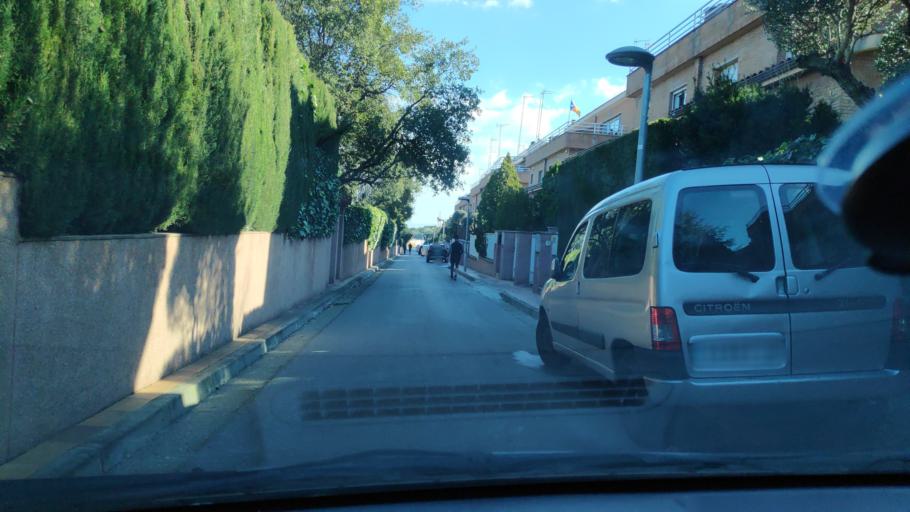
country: ES
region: Catalonia
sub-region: Provincia de Barcelona
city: Sant Quirze del Valles
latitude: 41.5243
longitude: 2.0708
